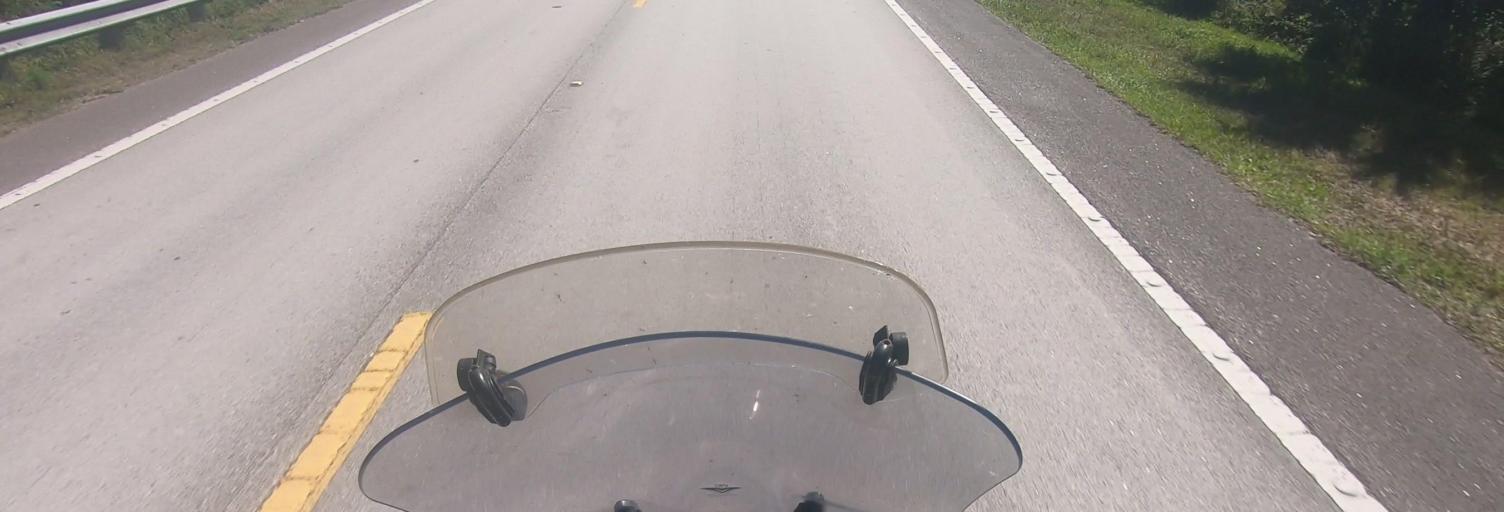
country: US
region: Florida
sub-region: Collier County
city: Marco
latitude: 25.8759
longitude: -81.2230
